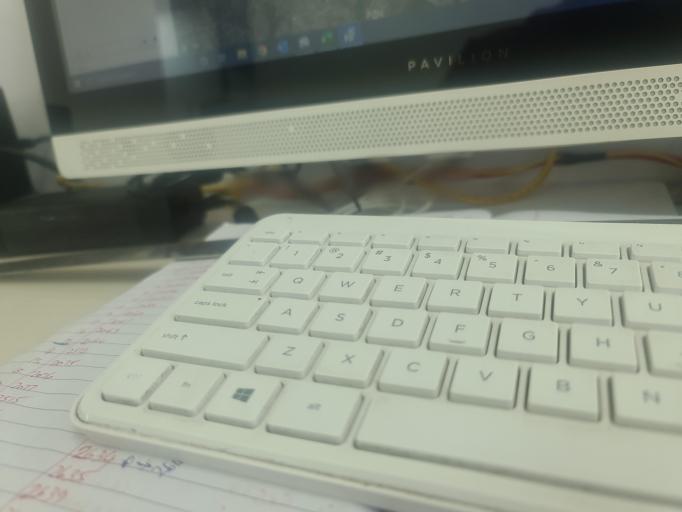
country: IN
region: Tamil Nadu
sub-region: Kancheepuram
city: Alandur
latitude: 13.0120
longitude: 80.2181
